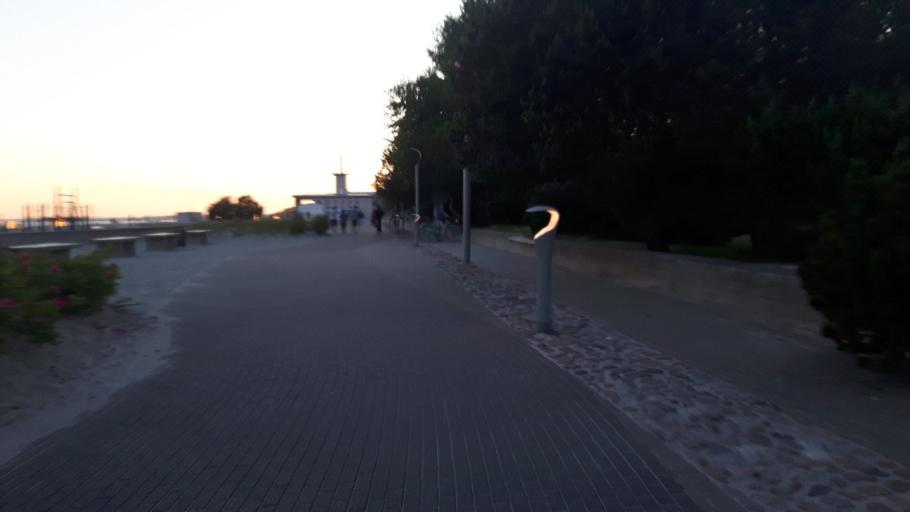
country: EE
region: Paernumaa
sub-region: Paernu linn
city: Parnu
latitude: 58.3731
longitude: 24.5024
